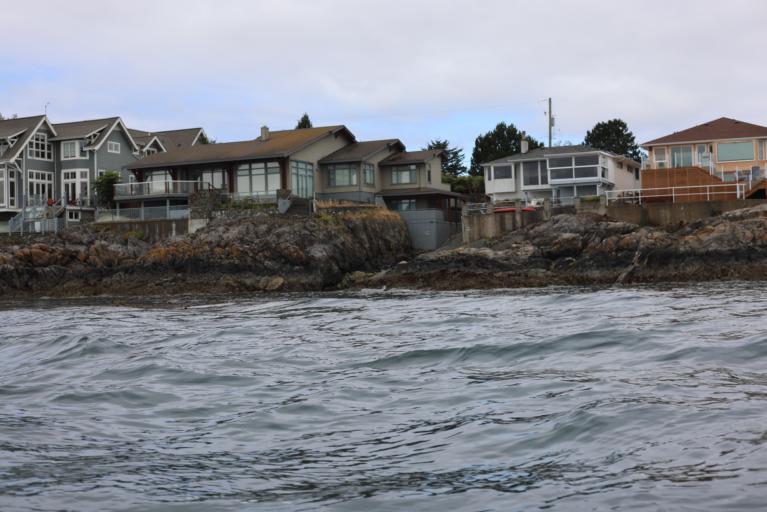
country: CA
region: British Columbia
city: Oak Bay
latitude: 48.4551
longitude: -123.2643
